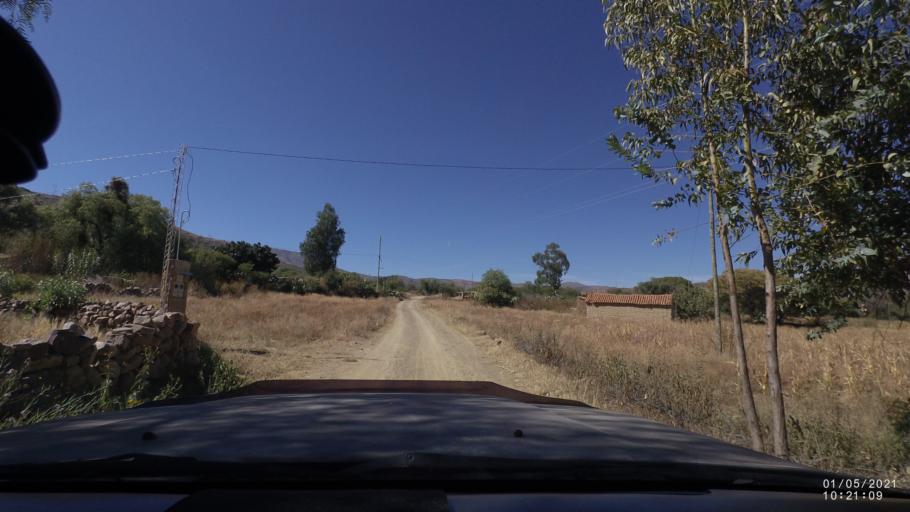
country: BO
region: Cochabamba
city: Capinota
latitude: -17.5640
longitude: -66.2026
